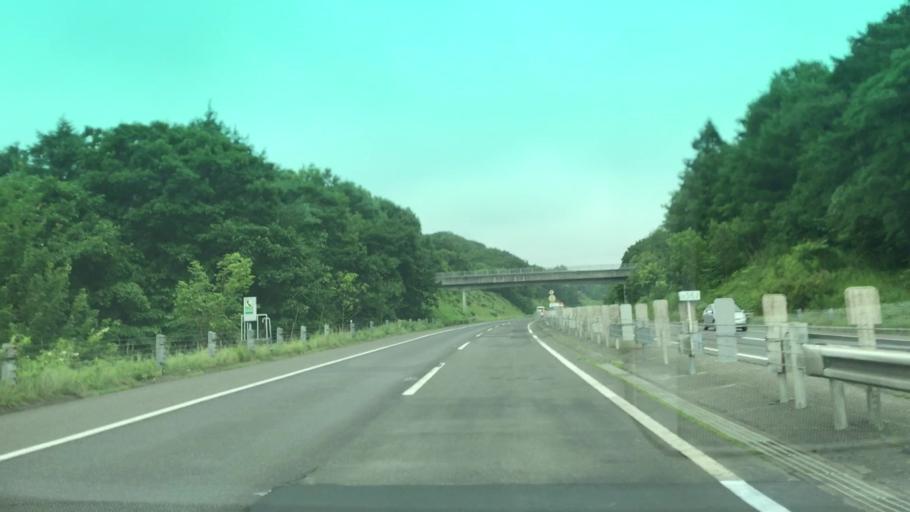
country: JP
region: Hokkaido
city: Tomakomai
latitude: 42.6611
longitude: 141.5802
